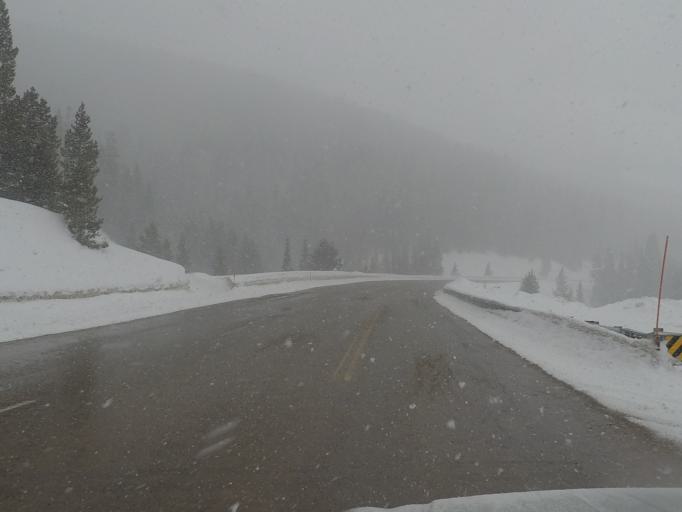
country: US
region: Montana
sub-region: Meagher County
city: White Sulphur Springs
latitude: 46.8344
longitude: -110.6955
